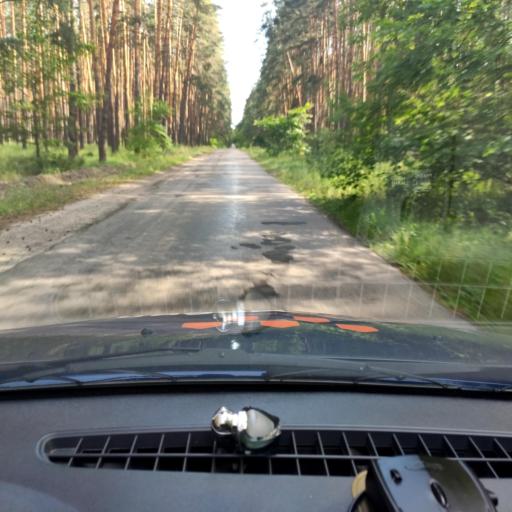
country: RU
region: Voronezj
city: Somovo
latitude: 51.7890
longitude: 39.4070
